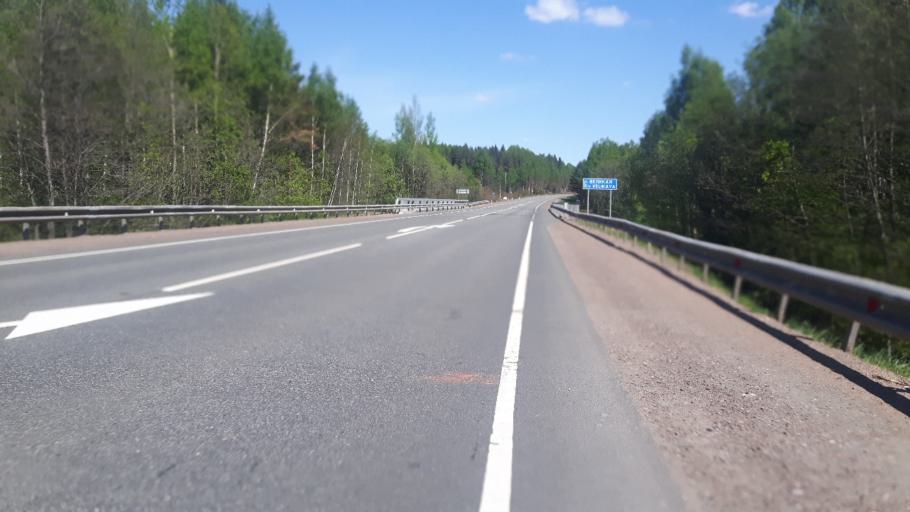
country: RU
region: Leningrad
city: Vysotsk
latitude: 60.6328
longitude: 28.2723
